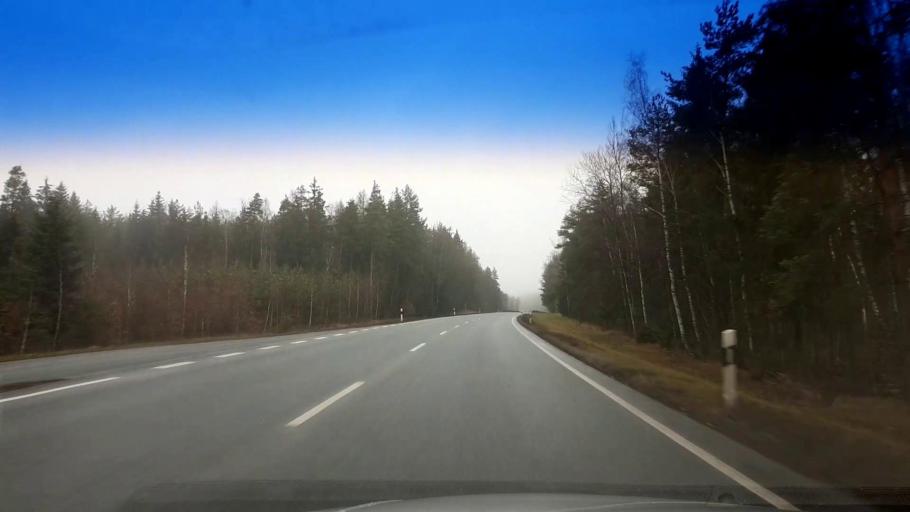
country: DE
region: Bavaria
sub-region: Upper Palatinate
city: Tirschenreuth
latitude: 49.8978
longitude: 12.3050
